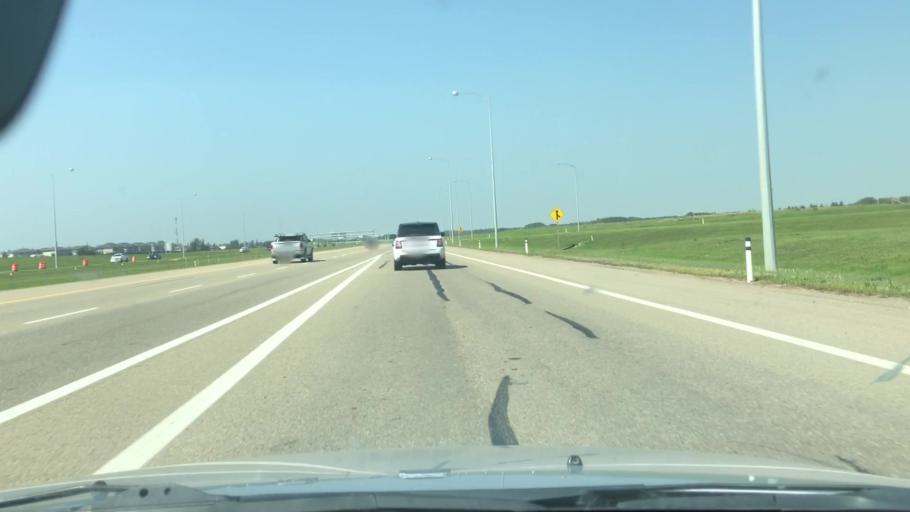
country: CA
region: Alberta
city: Edmonton
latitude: 53.6472
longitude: -113.4928
